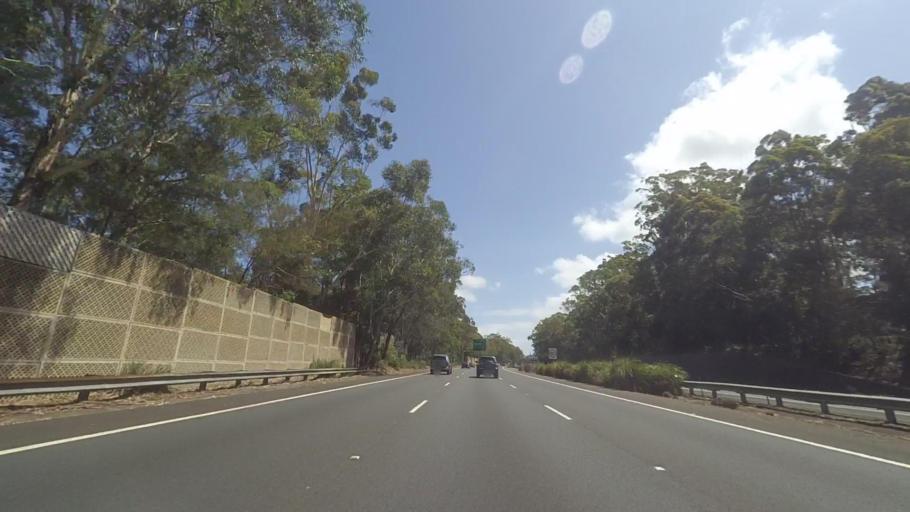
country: AU
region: New South Wales
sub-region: Ku-ring-gai
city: North Wahroonga
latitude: -33.7111
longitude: 151.1160
